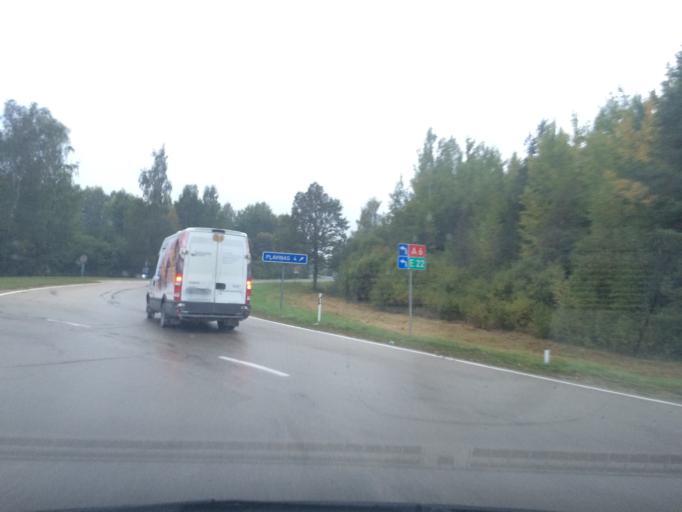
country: LV
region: Plavinu
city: Plavinas
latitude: 56.6157
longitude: 25.7836
